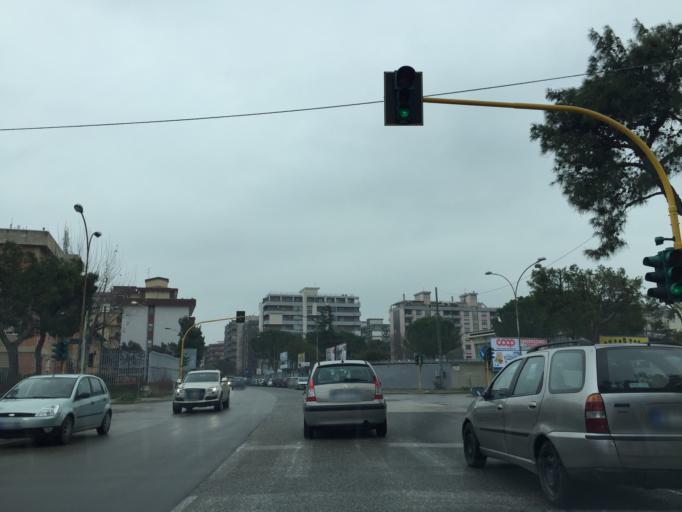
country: IT
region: Apulia
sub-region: Provincia di Foggia
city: Foggia
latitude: 41.4621
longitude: 15.5330
